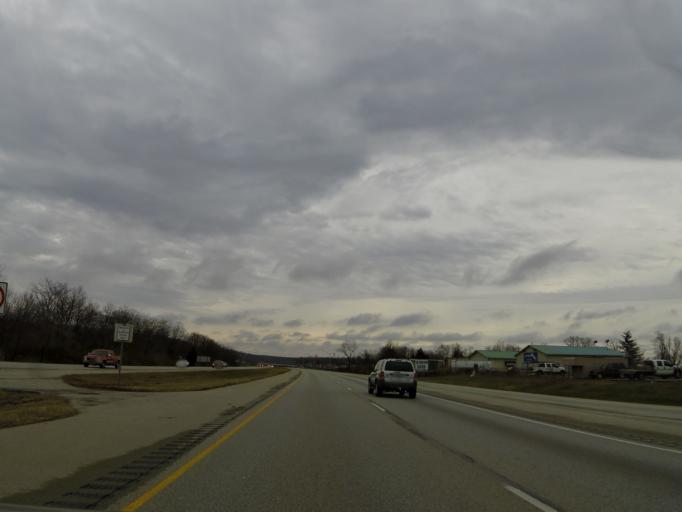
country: US
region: Ohio
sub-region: Hamilton County
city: Harrison
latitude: 39.2468
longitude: -84.7818
